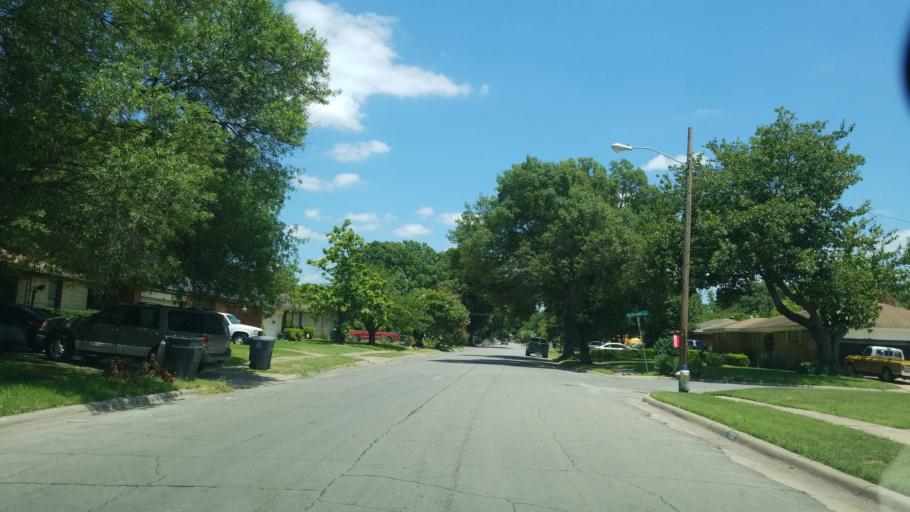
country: US
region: Texas
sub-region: Dallas County
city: Balch Springs
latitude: 32.7375
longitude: -96.7074
